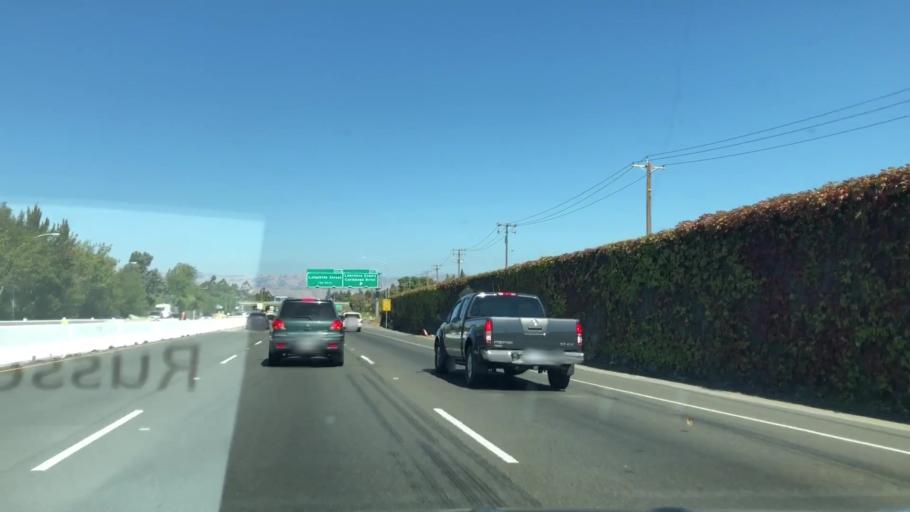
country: US
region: California
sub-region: Santa Clara County
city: Sunnyvale
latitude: 37.4074
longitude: -122.0051
